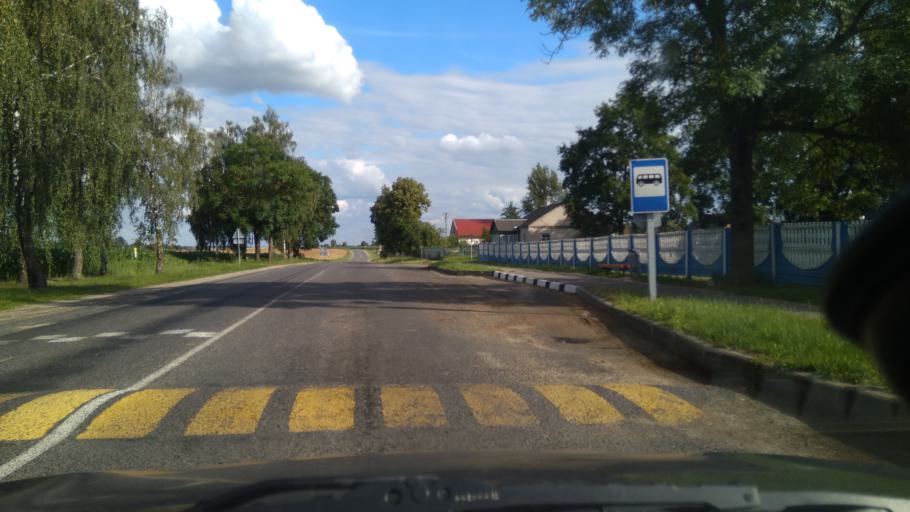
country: BY
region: Grodnenskaya
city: Masty
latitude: 53.3202
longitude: 24.6866
